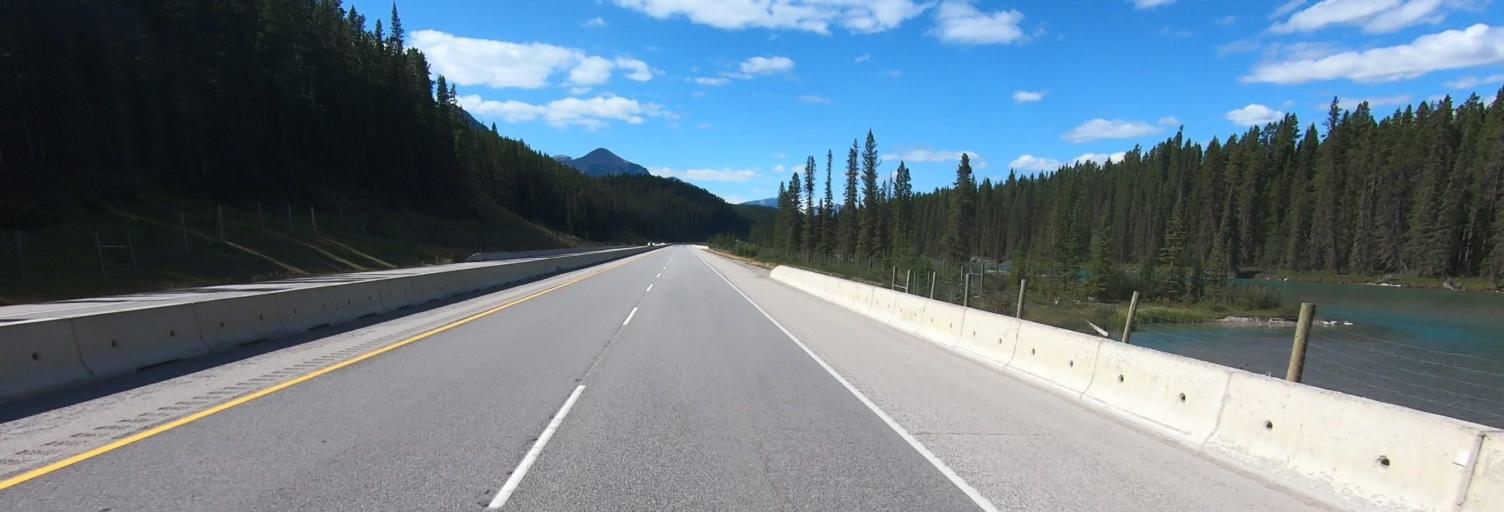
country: CA
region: Alberta
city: Lake Louise
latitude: 51.3495
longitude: -116.0816
